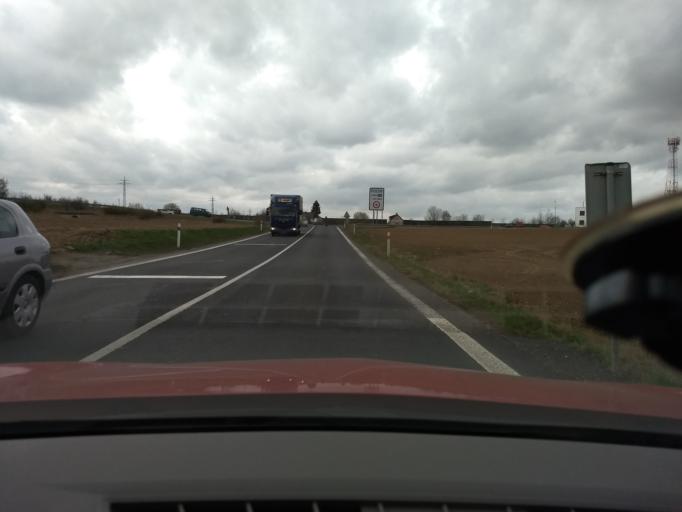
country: CZ
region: Central Bohemia
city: Unhost'
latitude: 50.1038
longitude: 14.1385
